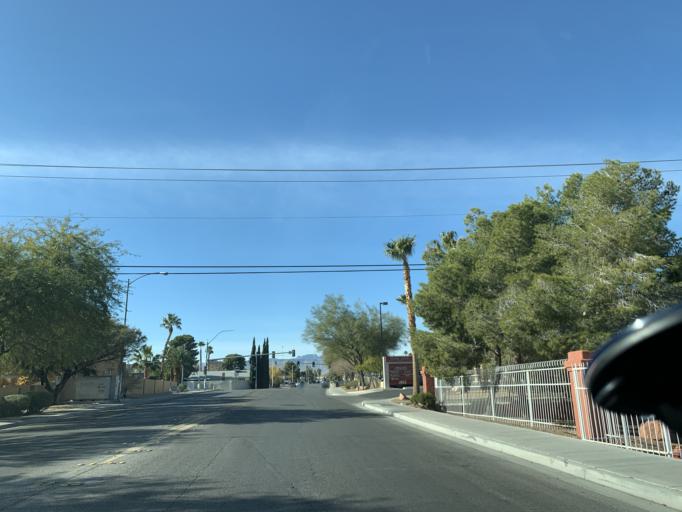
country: US
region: Nevada
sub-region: Clark County
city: Spring Valley
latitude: 36.0964
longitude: -115.2237
